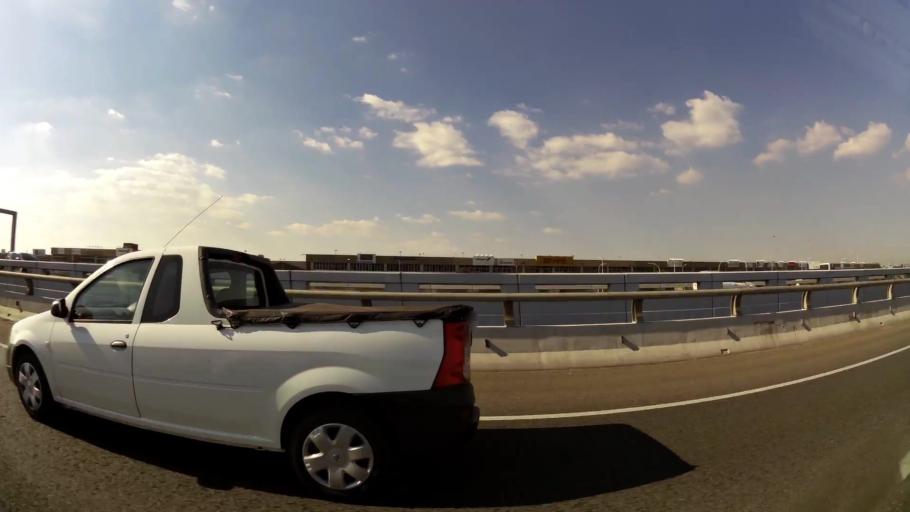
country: ZA
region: Gauteng
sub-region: City of Johannesburg Metropolitan Municipality
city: Modderfontein
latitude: -26.1098
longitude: 28.2393
